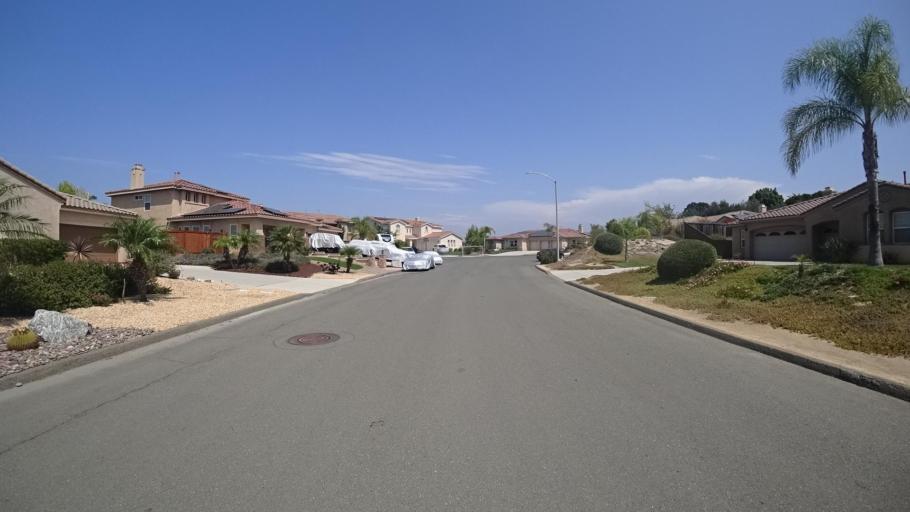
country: US
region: California
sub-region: San Diego County
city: Fallbrook
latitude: 33.3499
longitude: -117.2354
